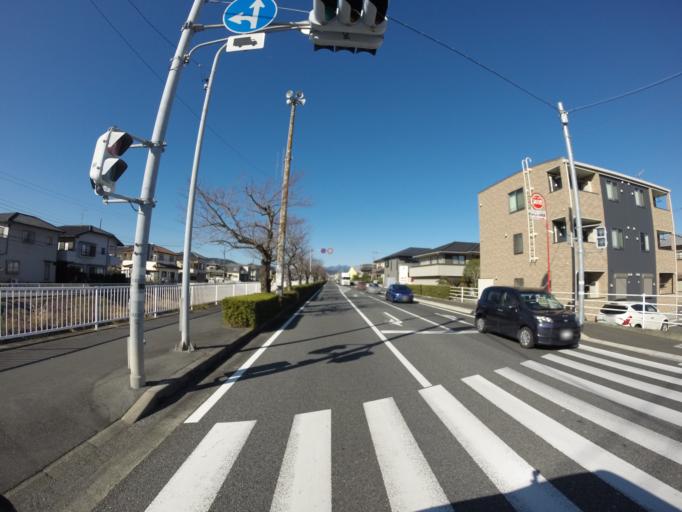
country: JP
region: Shizuoka
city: Fuji
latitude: 35.1363
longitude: 138.6524
